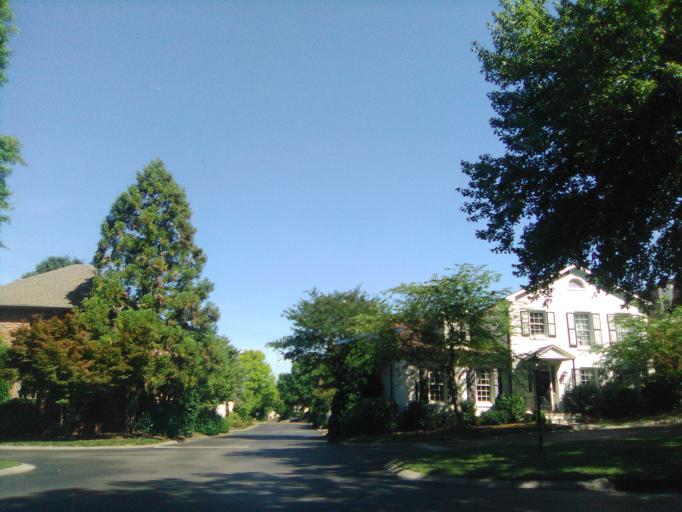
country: US
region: Tennessee
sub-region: Davidson County
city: Belle Meade
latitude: 36.1176
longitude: -86.8422
